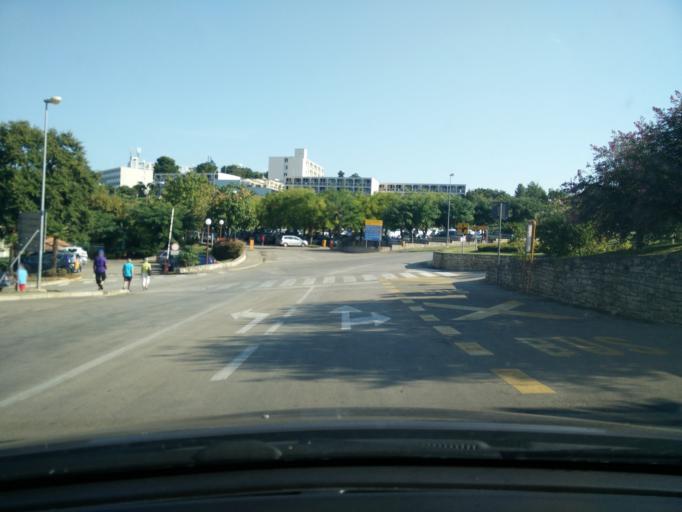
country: HR
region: Istarska
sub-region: Grad Porec
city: Porec
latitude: 45.1976
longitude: 13.5918
